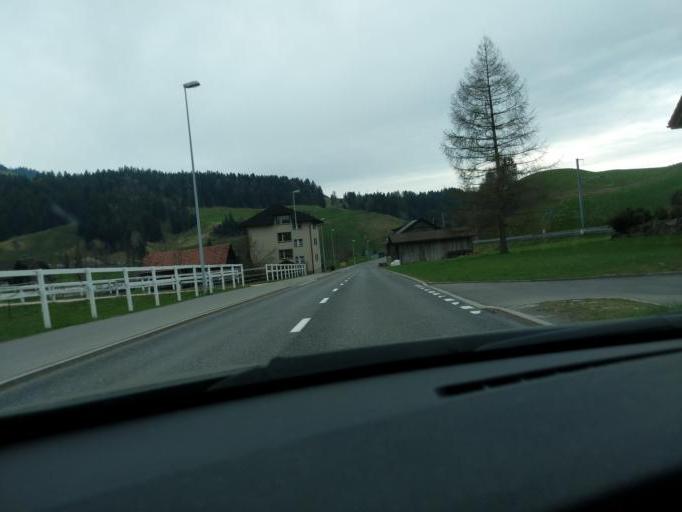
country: CH
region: Lucerne
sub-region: Entlebuch District
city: Escholzmatt
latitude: 46.9064
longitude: 7.9304
